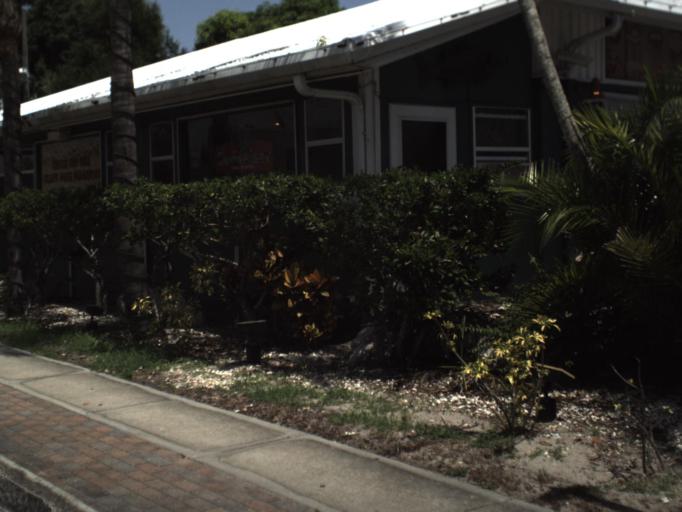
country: US
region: Florida
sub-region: Pinellas County
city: Tarpon Springs
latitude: 28.1520
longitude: -82.7568
